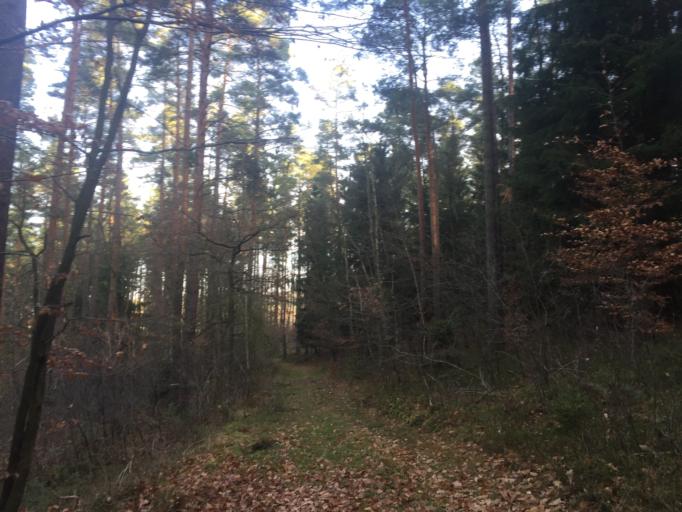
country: DE
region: Thuringia
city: Freienorla
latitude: 50.7540
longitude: 11.5371
